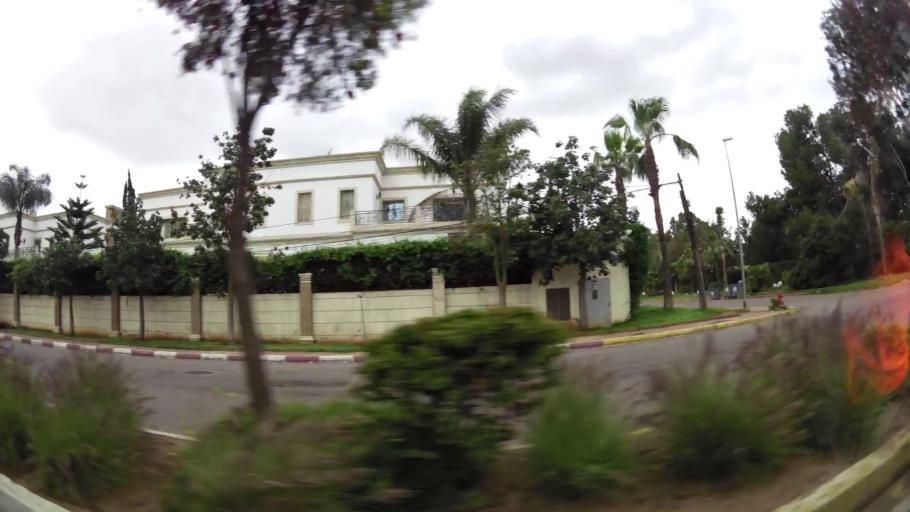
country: MA
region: Grand Casablanca
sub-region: Casablanca
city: Casablanca
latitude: 33.5245
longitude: -7.6315
